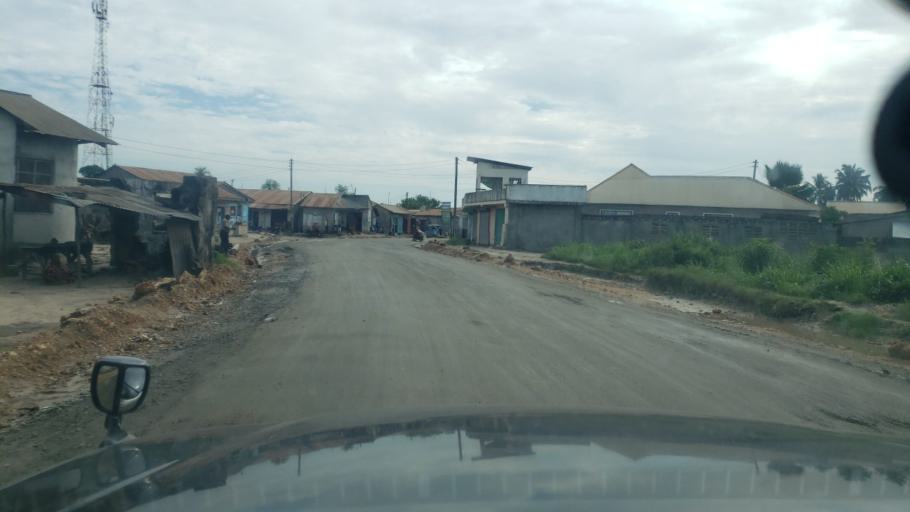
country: TZ
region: Pwani
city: Vikindu
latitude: -6.9274
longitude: 39.2541
